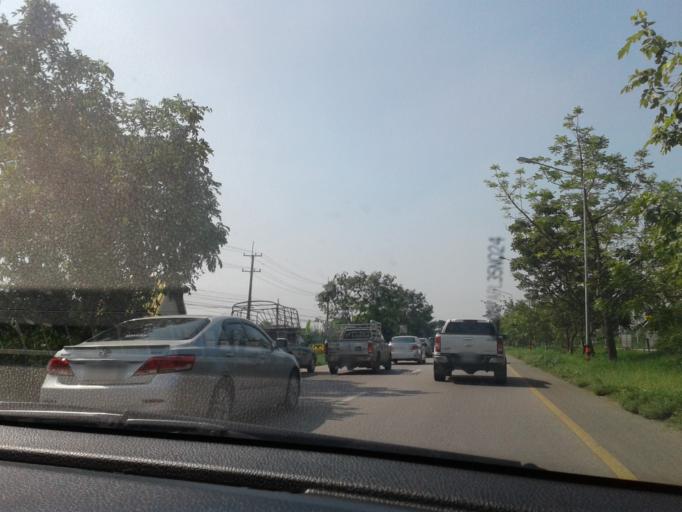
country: TH
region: Ratchaburi
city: Ban Pong
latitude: 13.7701
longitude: 99.9321
